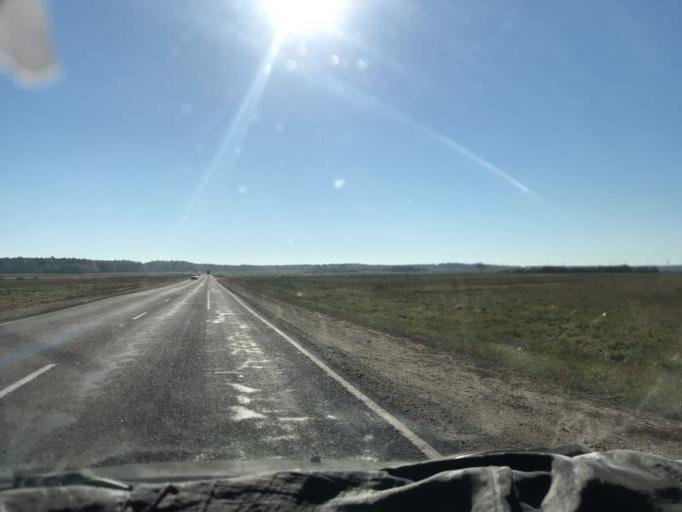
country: BY
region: Mogilev
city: Babruysk
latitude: 53.0681
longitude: 29.0776
